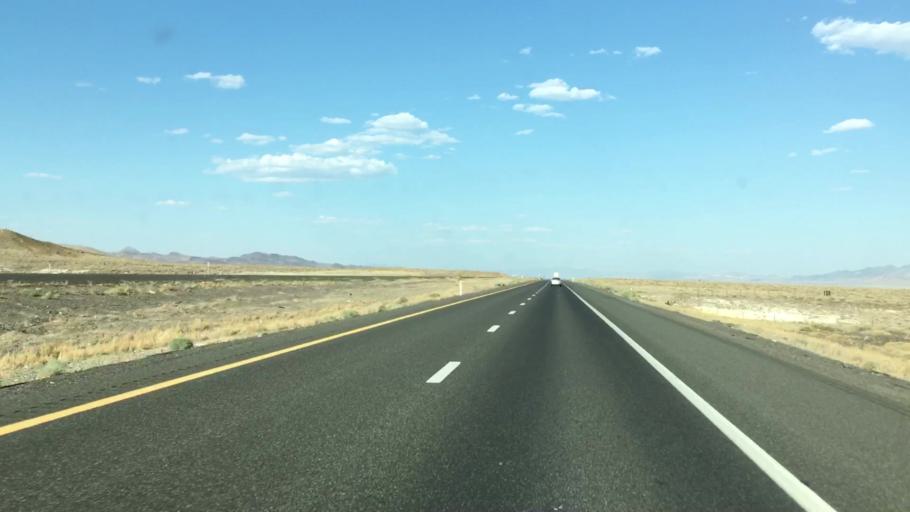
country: US
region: Nevada
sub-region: Churchill County
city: Fallon
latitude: 39.8648
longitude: -118.9011
